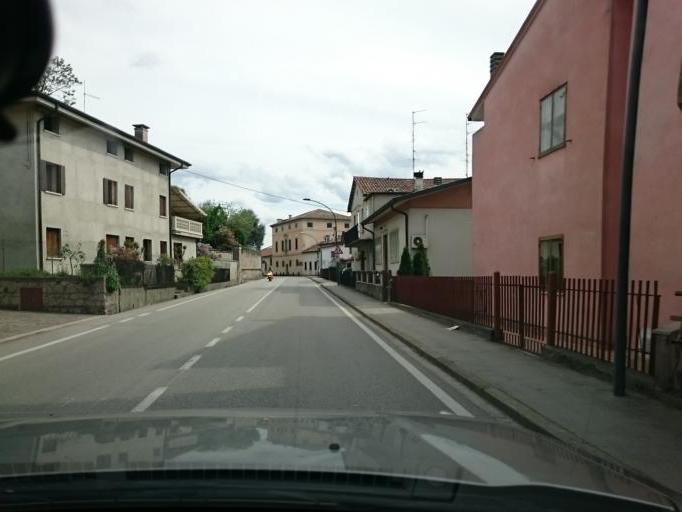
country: IT
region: Veneto
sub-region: Provincia di Vicenza
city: Montegalda
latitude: 45.4450
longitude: 11.6718
